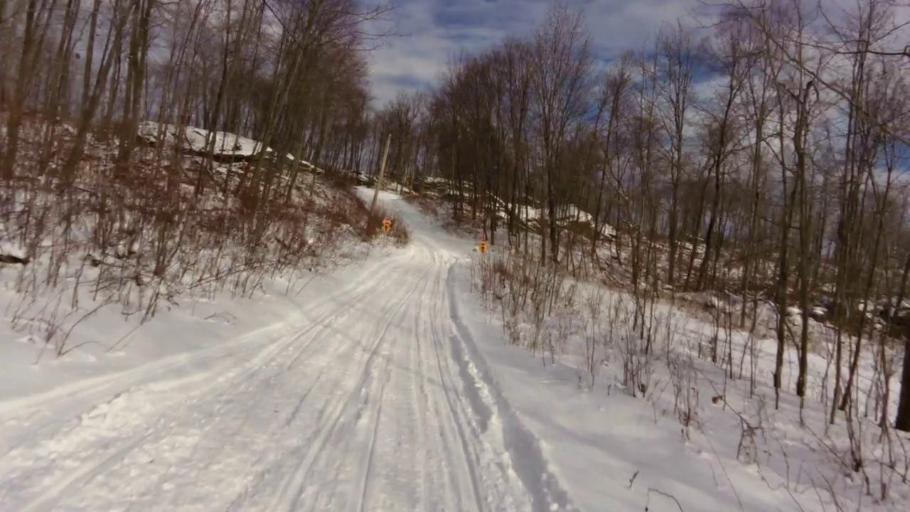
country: US
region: Pennsylvania
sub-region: McKean County
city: Foster Brook
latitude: 42.0060
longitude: -78.5877
